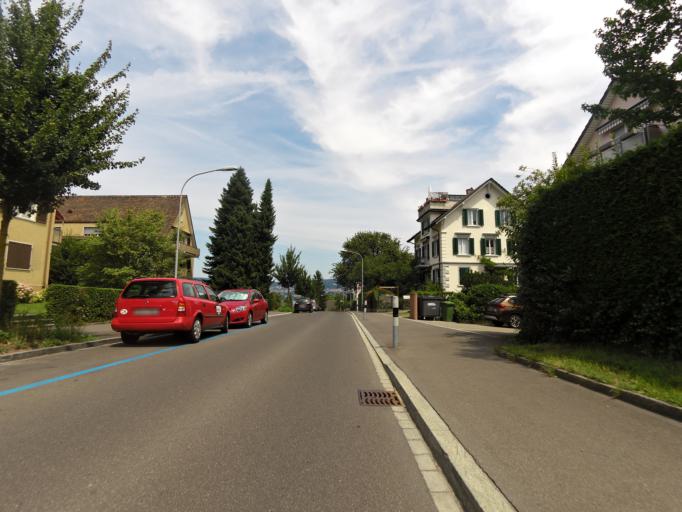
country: CH
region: Zurich
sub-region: Bezirk Zuerich
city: Zuerich (Kreis 2) / Wollishofen
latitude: 47.3367
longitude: 8.5335
